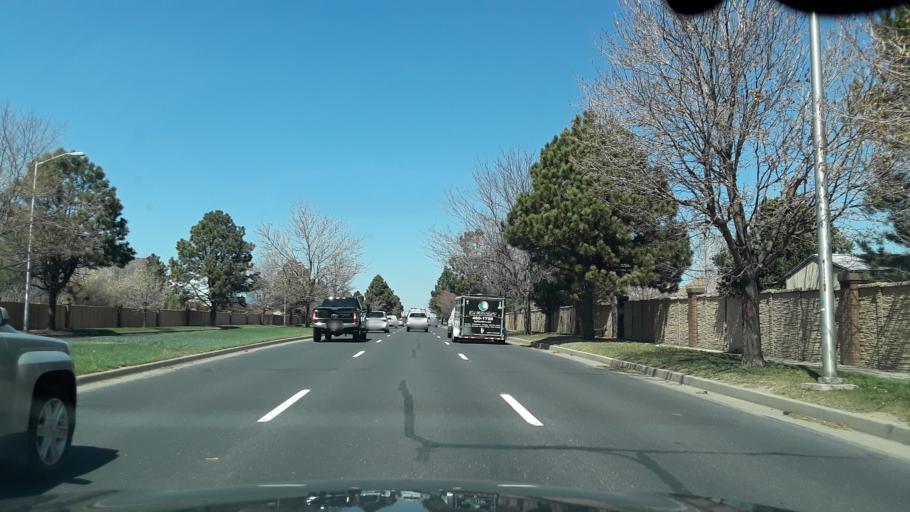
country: US
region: Colorado
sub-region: El Paso County
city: Cimarron Hills
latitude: 38.9172
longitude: -104.7356
